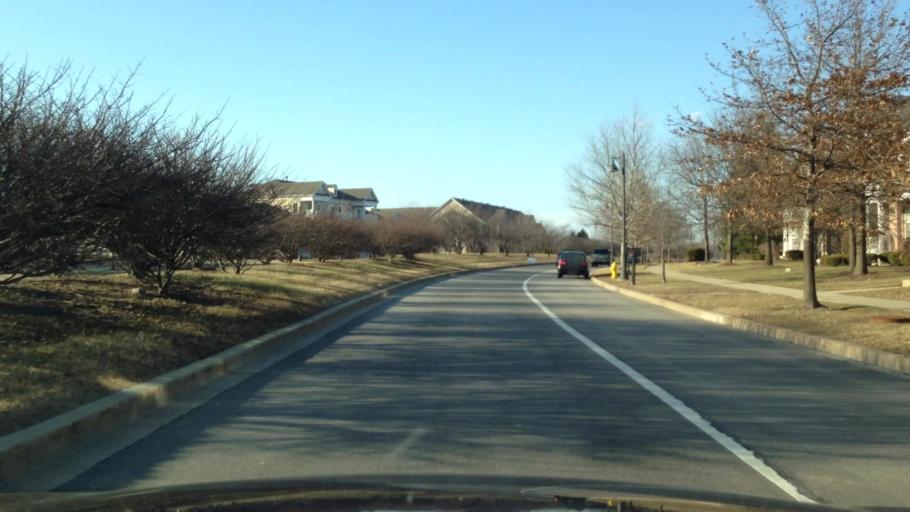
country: US
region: Illinois
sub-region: Cook County
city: Glenview
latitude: 42.0837
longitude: -87.8207
